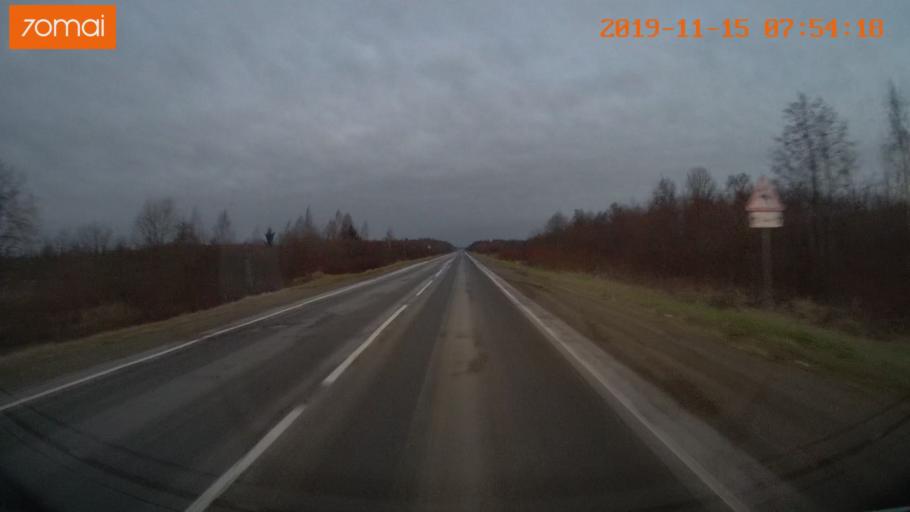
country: RU
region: Vologda
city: Cherepovets
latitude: 58.8973
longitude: 38.1774
